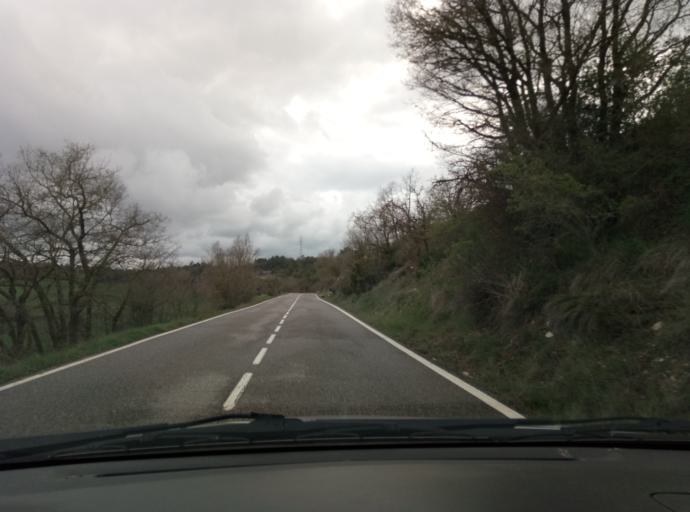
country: ES
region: Catalonia
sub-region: Provincia de Tarragona
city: Santa Coloma de Queralt
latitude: 41.5416
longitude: 1.3520
